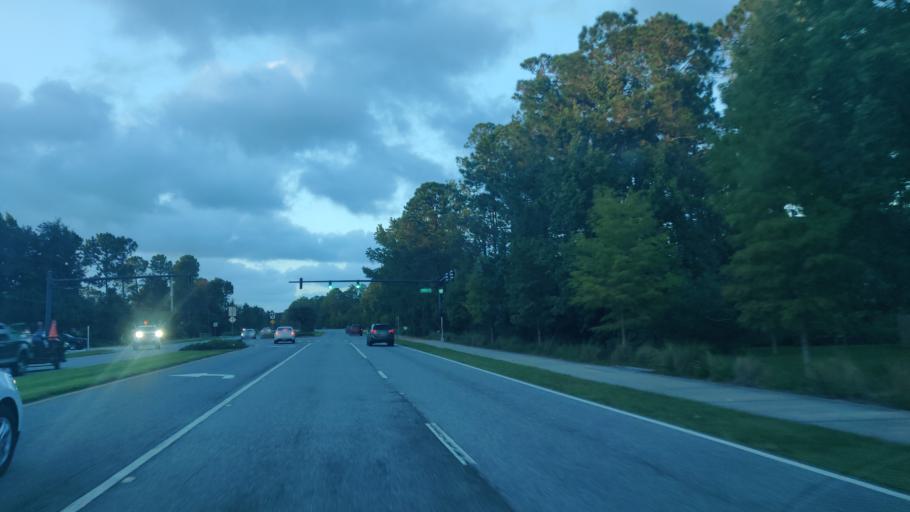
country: US
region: Florida
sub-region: Flagler County
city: Bunnell
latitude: 29.5047
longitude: -81.2198
